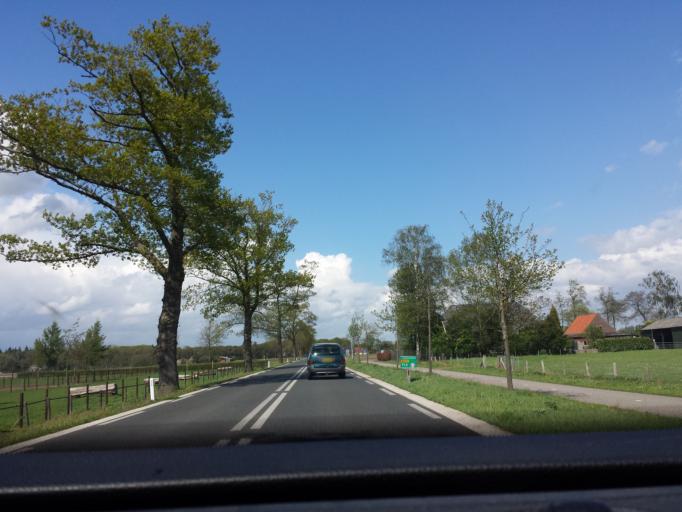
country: NL
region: Gelderland
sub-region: Gemeente Bronckhorst
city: Zelhem
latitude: 52.0373
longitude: 6.4090
